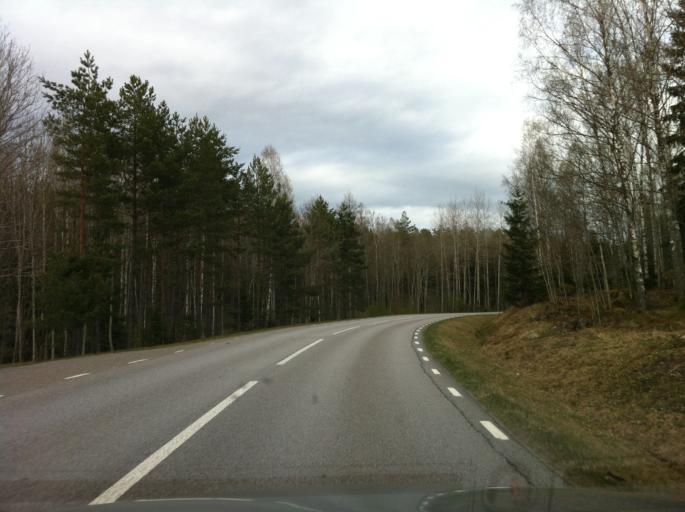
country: SE
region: OEstergoetland
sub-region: Kinda Kommun
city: Rimforsa
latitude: 58.0900
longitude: 15.8545
